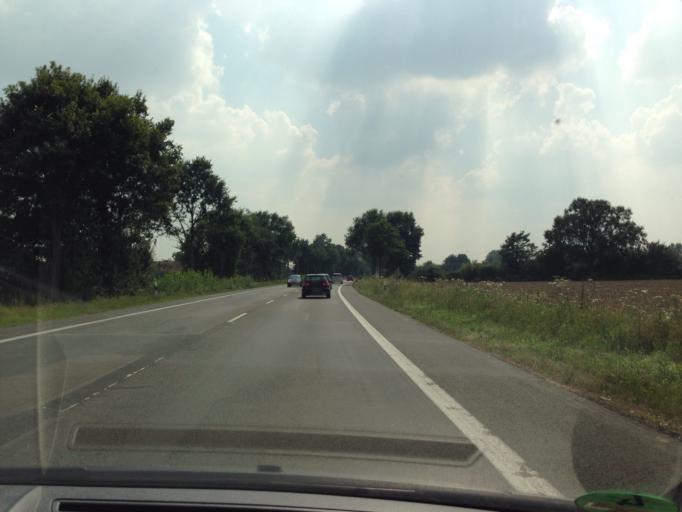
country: DE
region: North Rhine-Westphalia
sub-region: Regierungsbezirk Munster
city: Muenster
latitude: 51.9855
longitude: 7.5363
